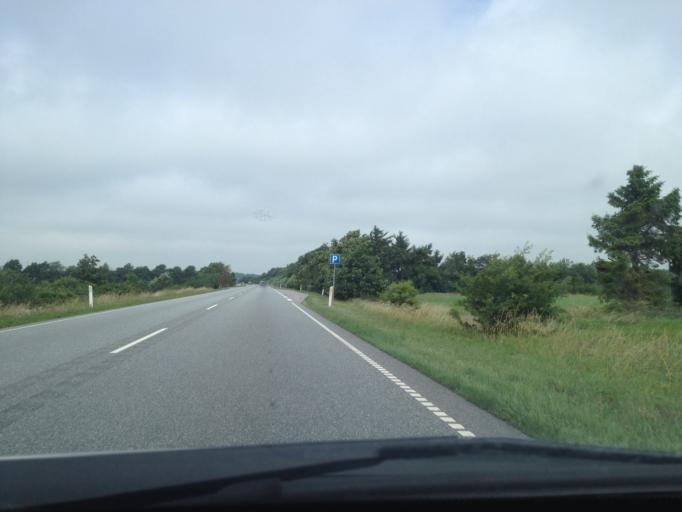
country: DK
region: South Denmark
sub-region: Esbjerg Kommune
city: Bramming
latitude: 55.4131
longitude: 8.7169
